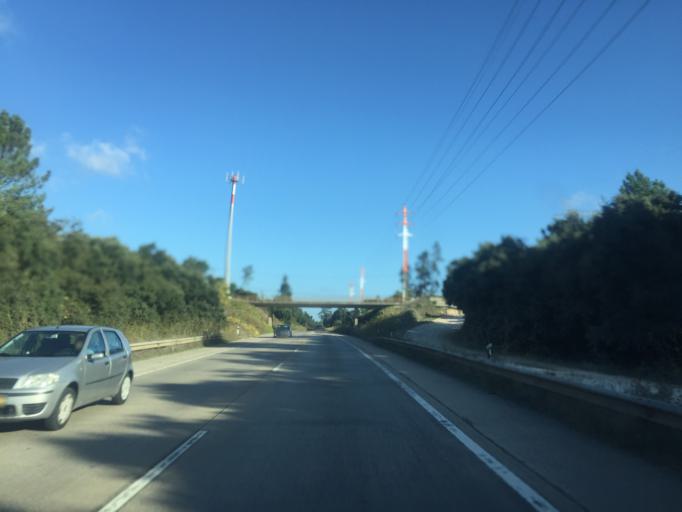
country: PT
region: Santarem
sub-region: Rio Maior
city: Rio Maior
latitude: 39.3613
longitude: -8.9684
